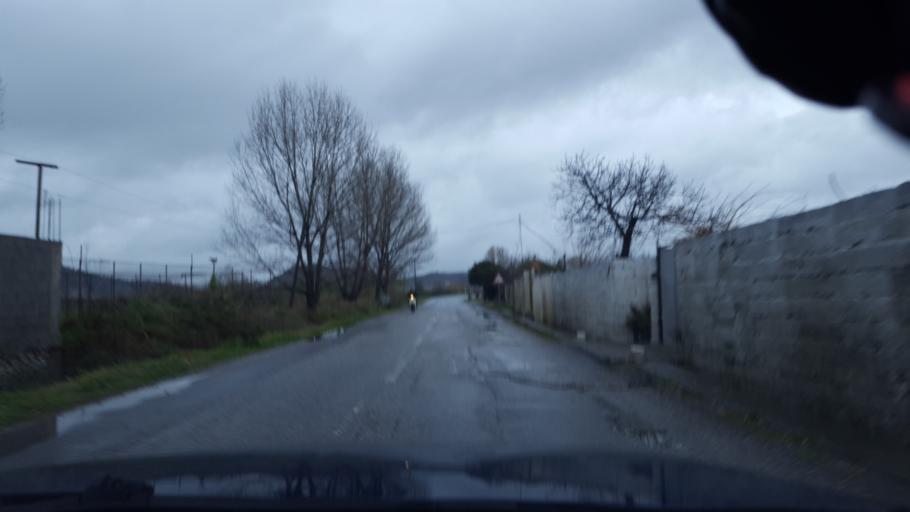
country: AL
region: Shkoder
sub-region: Rrethi i Shkodres
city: Berdica e Madhe
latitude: 42.0246
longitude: 19.4873
